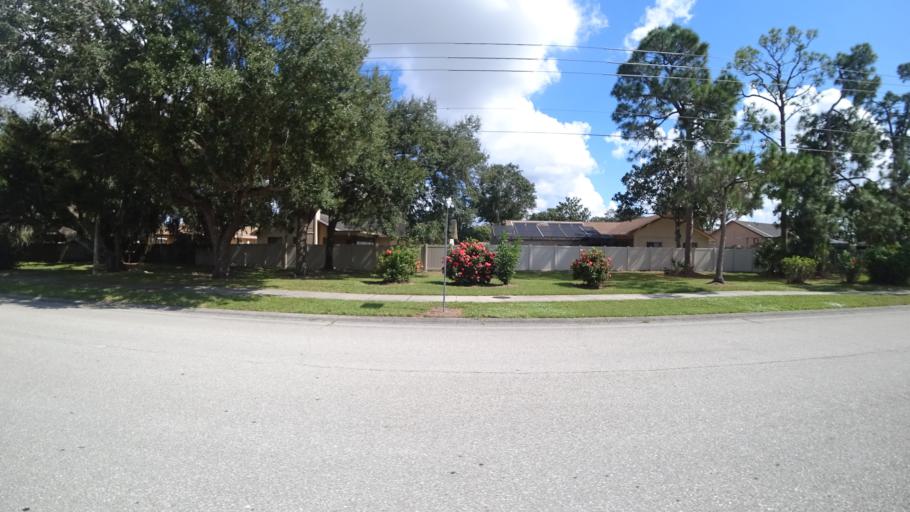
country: US
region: Florida
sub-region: Manatee County
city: Whitfield
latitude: 27.4168
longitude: -82.5550
